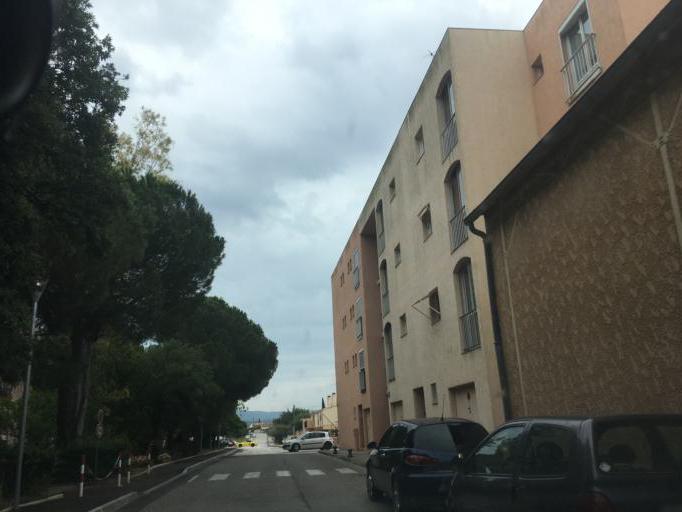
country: FR
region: Provence-Alpes-Cote d'Azur
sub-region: Departement du Var
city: La Londe-les-Maures
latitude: 43.1407
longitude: 6.2333
